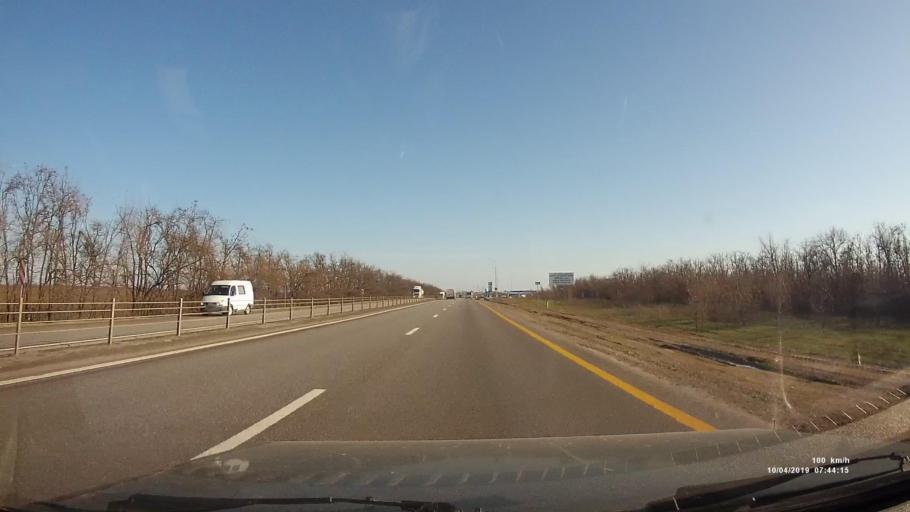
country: RU
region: Rostov
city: Likhoy
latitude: 48.1752
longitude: 40.2643
